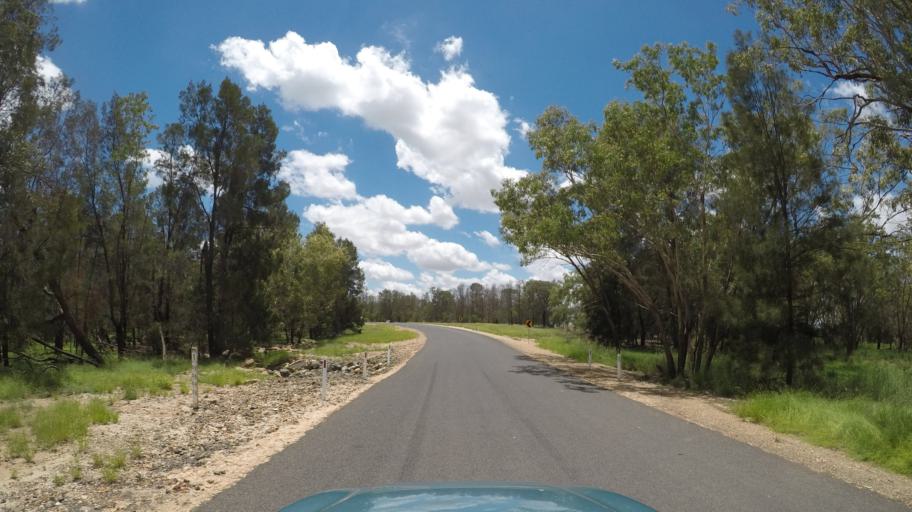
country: AU
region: Queensland
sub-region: Goondiwindi
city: Goondiwindi
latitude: -28.1500
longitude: 150.1273
